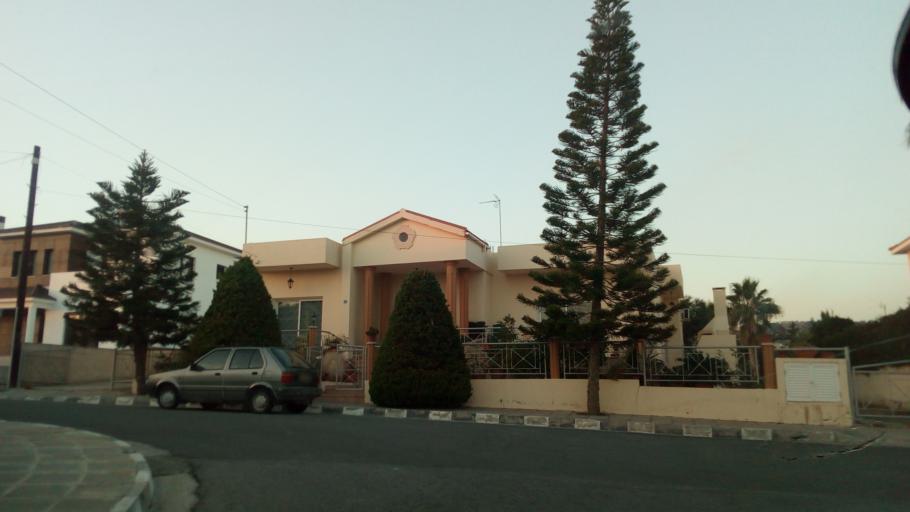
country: CY
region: Larnaka
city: Kofinou
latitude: 34.8562
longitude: 33.4596
